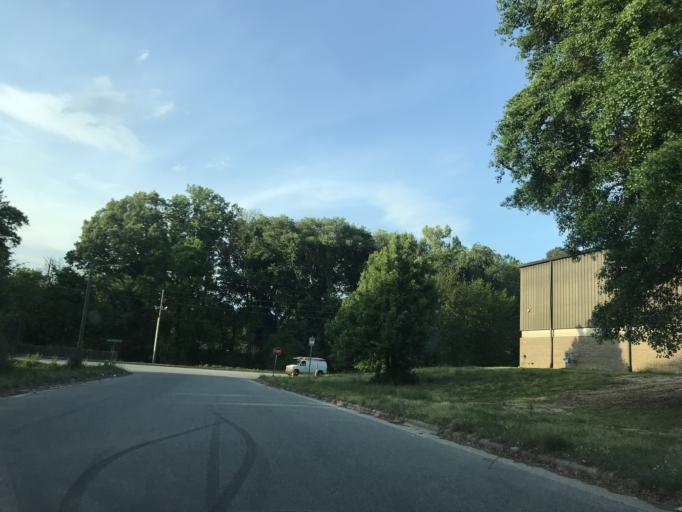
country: US
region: North Carolina
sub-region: Wake County
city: Raleigh
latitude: 35.8011
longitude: -78.5807
